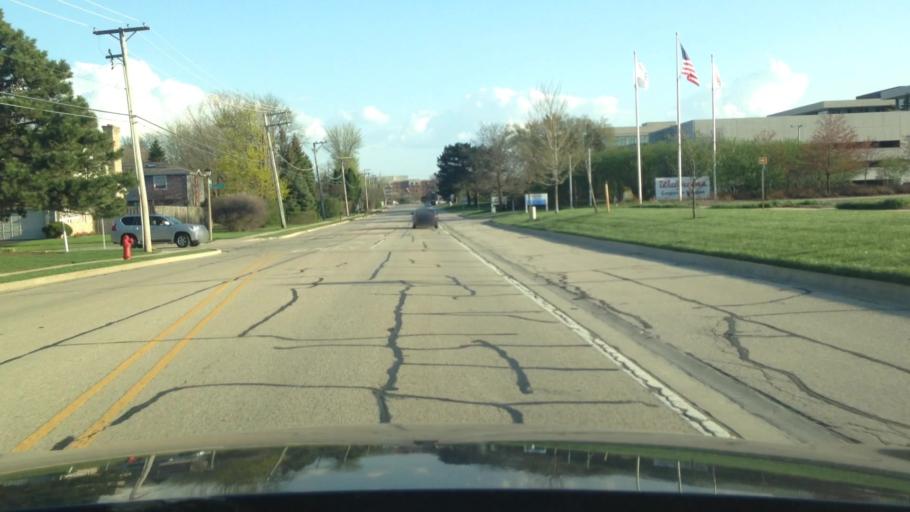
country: US
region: Illinois
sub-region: Lake County
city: Deerfield
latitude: 42.1570
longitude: -87.8674
